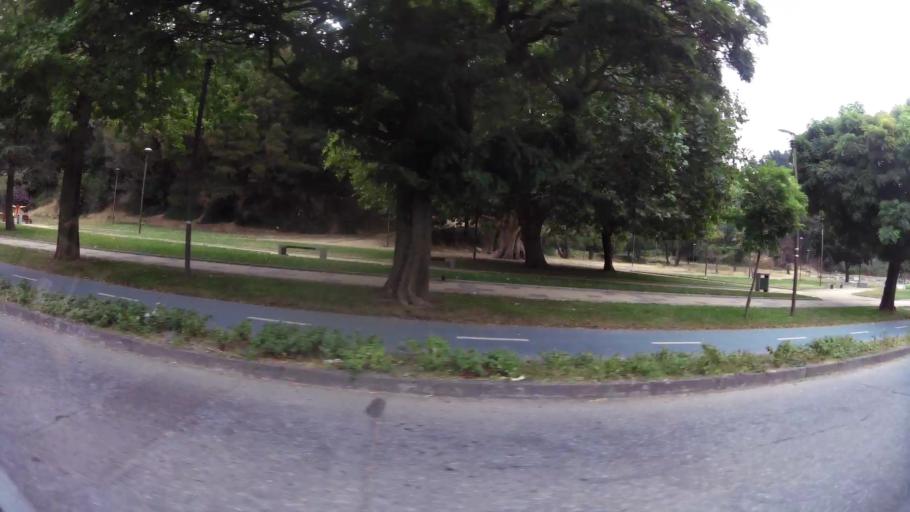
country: CL
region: Biobio
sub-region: Provincia de Concepcion
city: Concepcion
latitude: -36.8343
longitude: -73.0534
